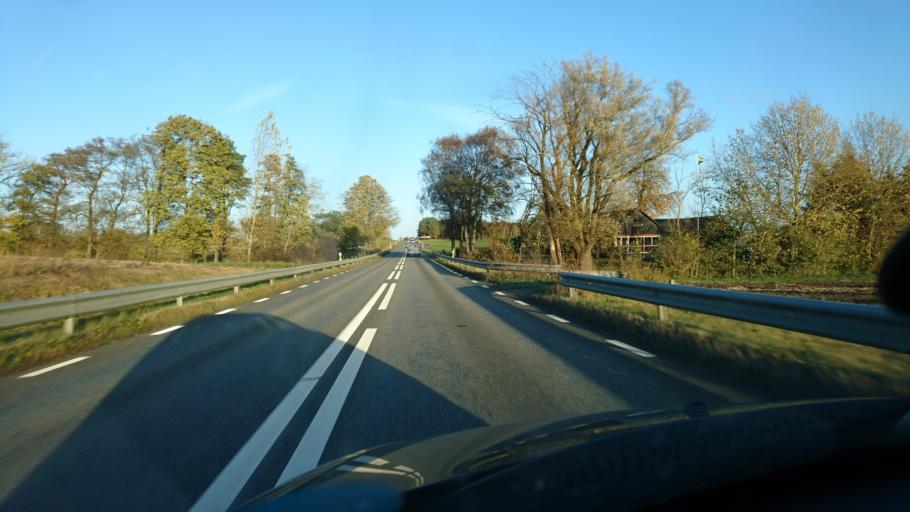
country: SE
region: Skane
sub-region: Tomelilla Kommun
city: Tomelilla
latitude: 55.5514
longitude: 14.0707
